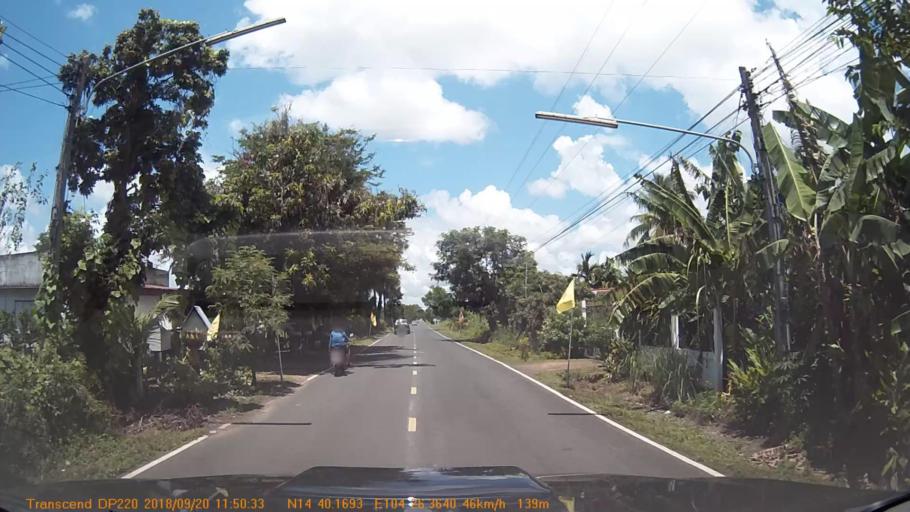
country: TH
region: Sisaket
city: Khun Han
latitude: 14.6697
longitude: 104.4393
